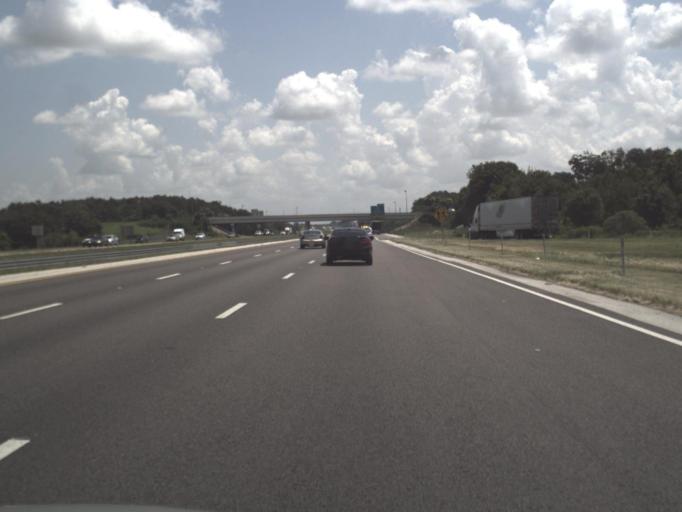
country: US
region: Florida
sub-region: Hillsborough County
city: Mango
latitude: 28.0025
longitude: -82.3228
